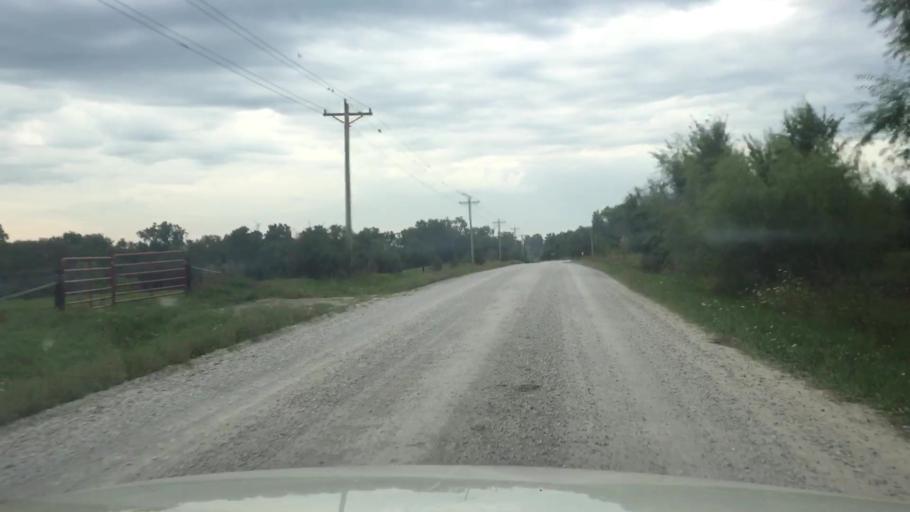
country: US
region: Iowa
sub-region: Story County
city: Huxley
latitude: 41.8961
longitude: -93.5810
